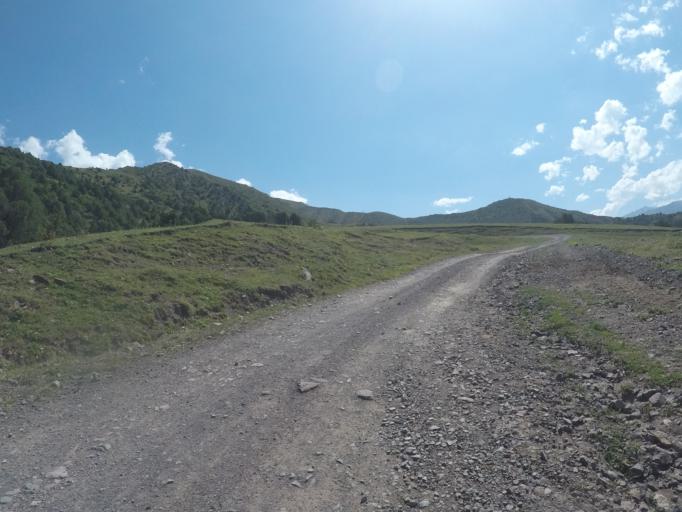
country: KG
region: Chuy
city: Bishkek
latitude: 42.6474
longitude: 74.5588
